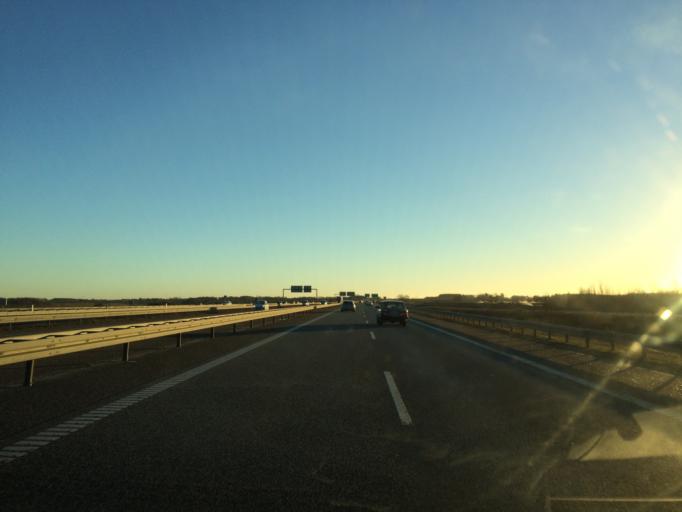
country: DK
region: Central Jutland
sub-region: Herning Kommune
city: Lind
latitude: 56.1239
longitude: 9.0121
